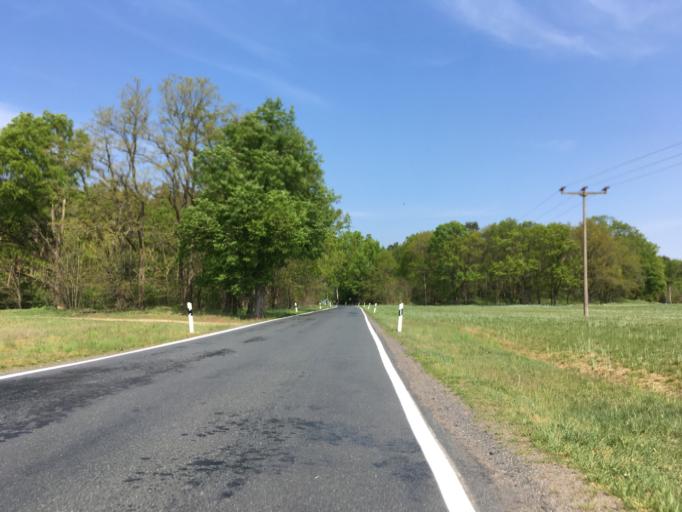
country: DE
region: Brandenburg
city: Melchow
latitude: 52.7228
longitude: 13.7124
